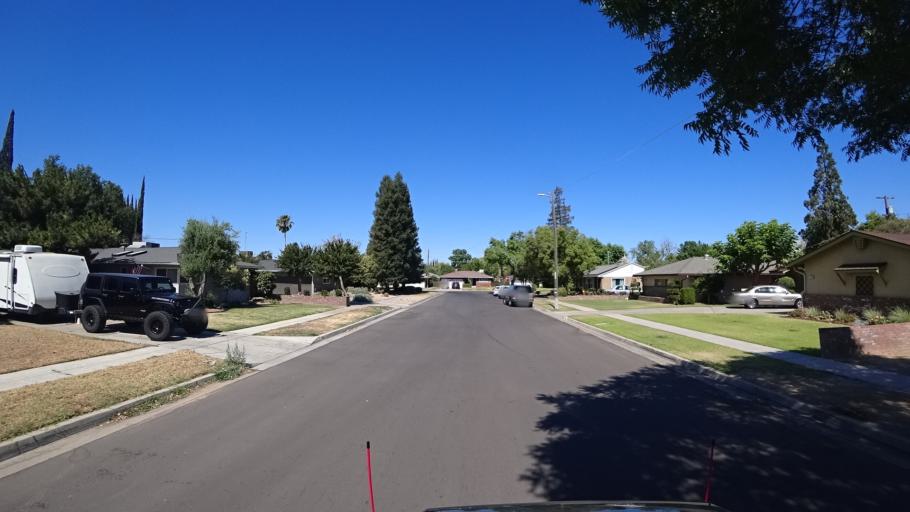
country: US
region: California
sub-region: Fresno County
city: Fresno
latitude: 36.7833
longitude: -119.8335
